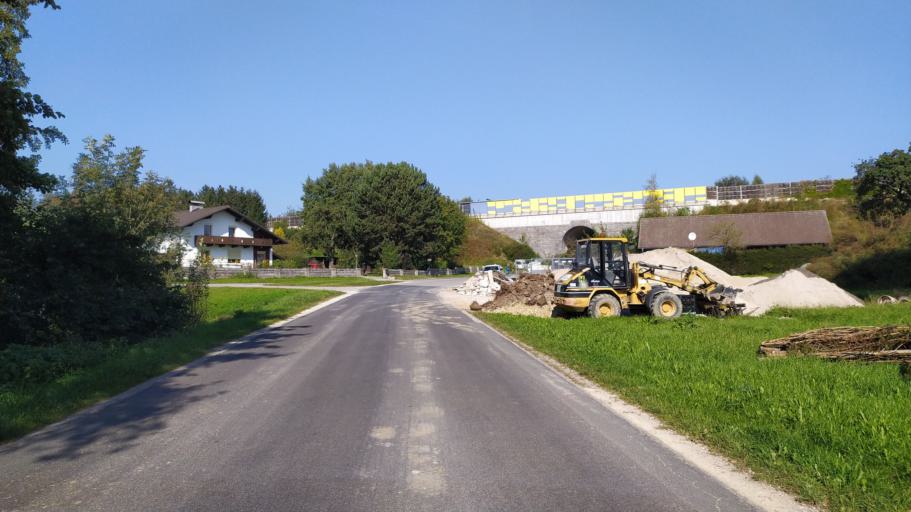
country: AT
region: Lower Austria
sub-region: Politischer Bezirk Amstetten
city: Zeillern
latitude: 48.1178
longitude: 14.7430
